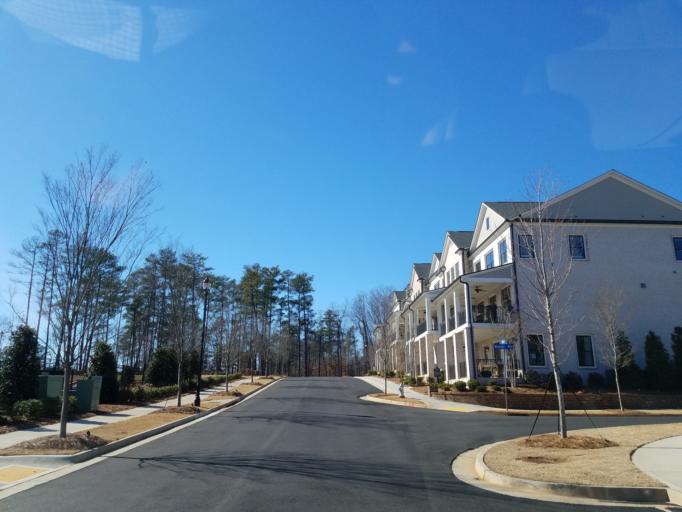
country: US
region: Georgia
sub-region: Fulton County
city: Alpharetta
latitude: 34.0524
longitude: -84.3169
